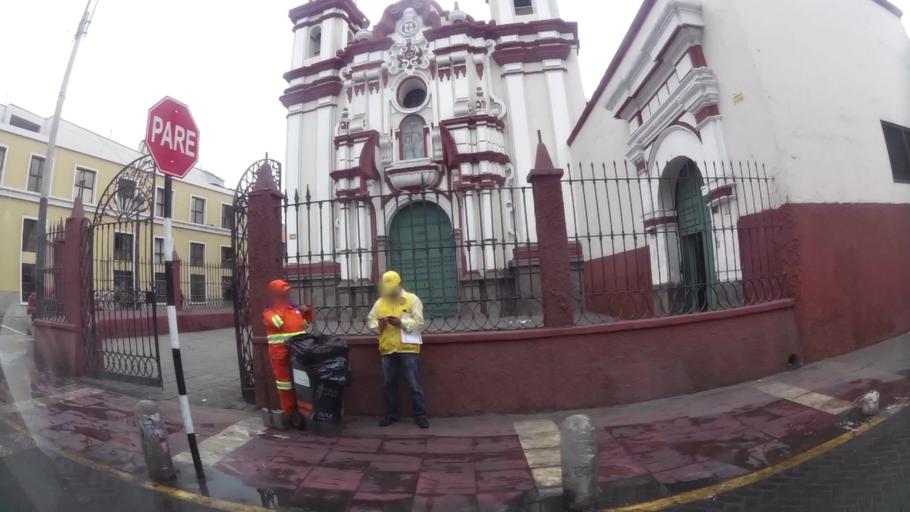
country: PE
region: Lima
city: Lima
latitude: -12.0474
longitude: -77.0229
